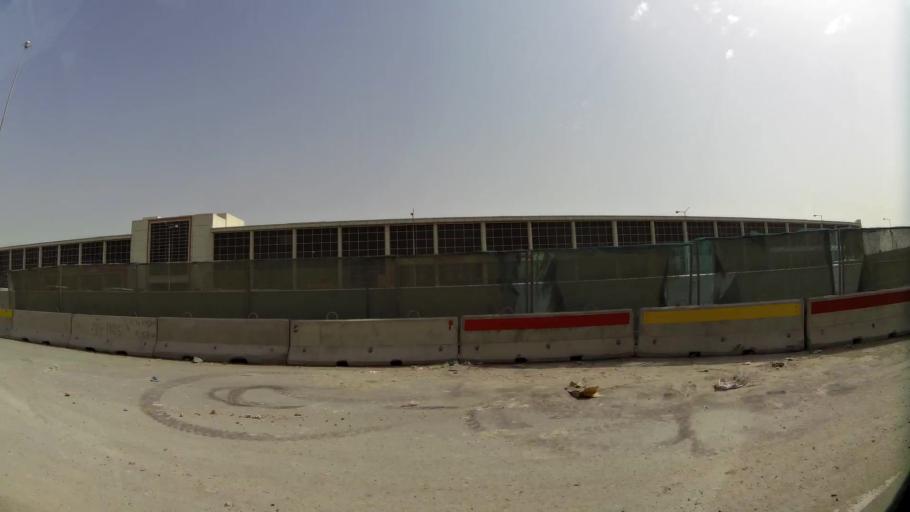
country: QA
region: Al Wakrah
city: Al Wukayr
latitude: 25.1945
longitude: 51.4536
